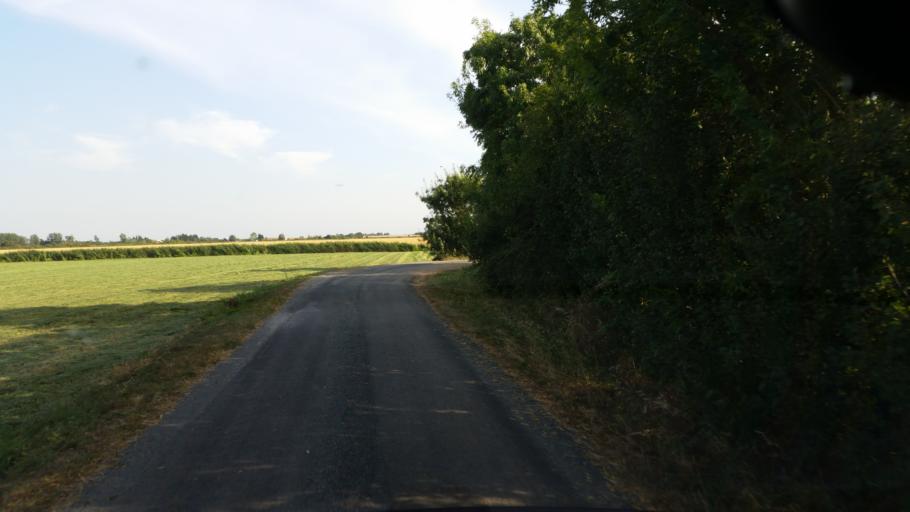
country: FR
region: Poitou-Charentes
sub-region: Departement de la Charente-Maritime
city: Marans
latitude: 46.3111
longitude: -0.9470
